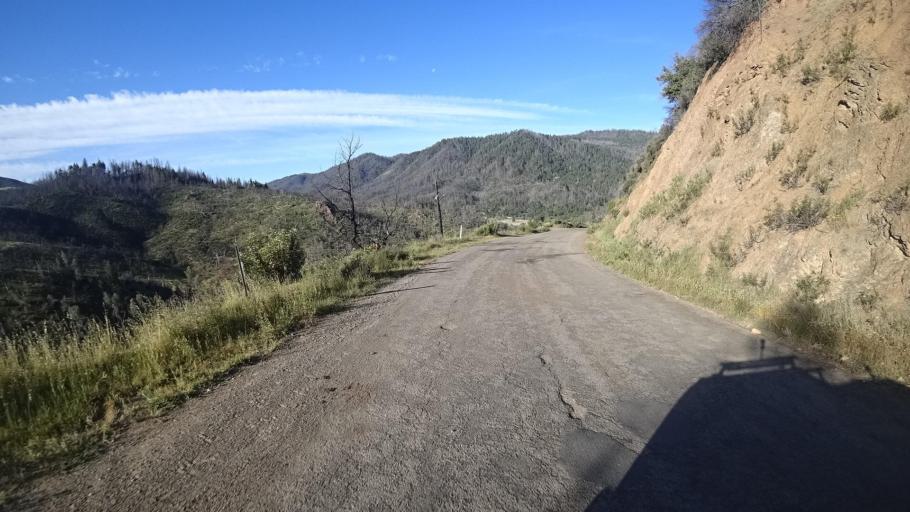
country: US
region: California
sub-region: Lake County
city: Upper Lake
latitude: 39.2584
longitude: -122.9436
